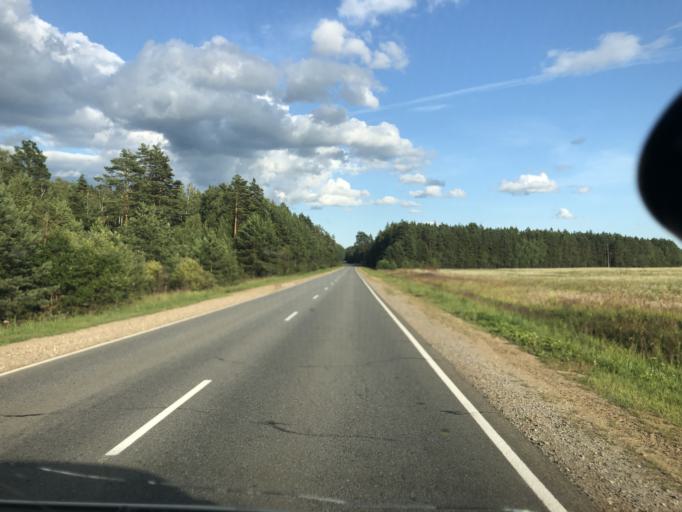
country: RU
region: Kaluga
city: Yukhnov
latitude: 54.7170
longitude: 35.2317
